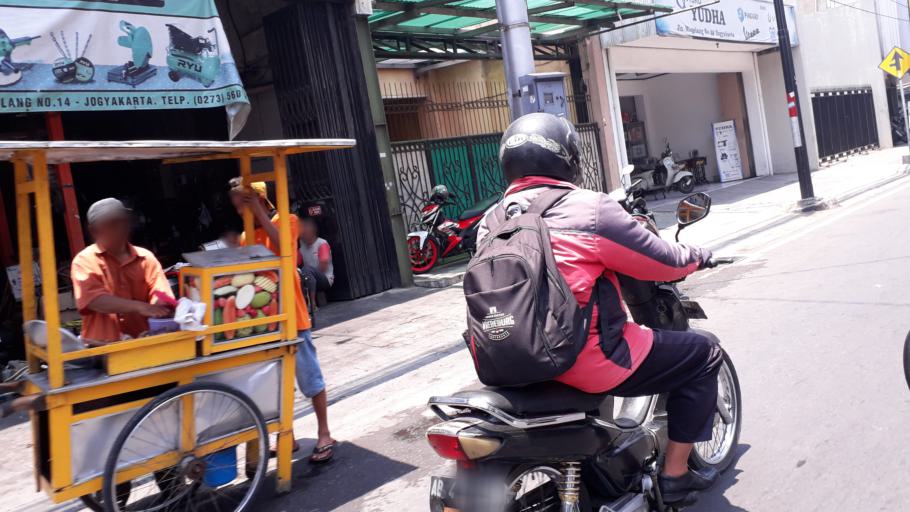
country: ID
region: Daerah Istimewa Yogyakarta
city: Yogyakarta
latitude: -7.7800
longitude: 110.3610
